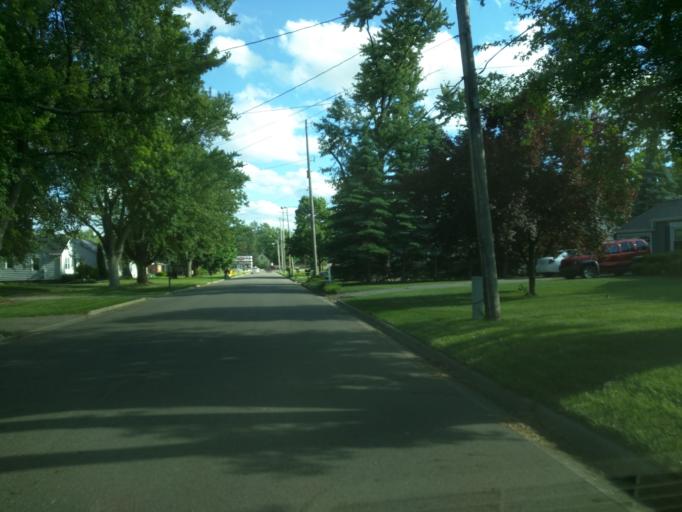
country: US
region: Michigan
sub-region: Eaton County
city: Waverly
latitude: 42.7430
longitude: -84.6168
